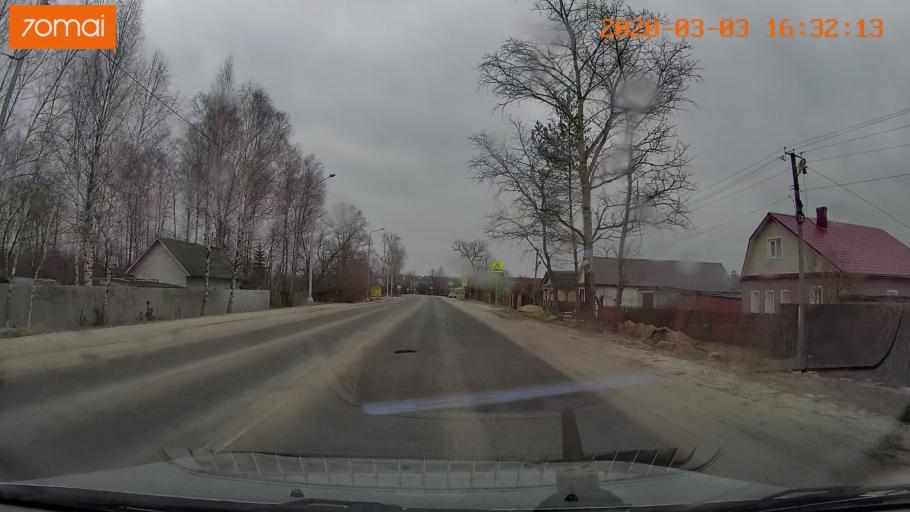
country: RU
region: Moskovskaya
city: Konobeyevo
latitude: 55.4215
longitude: 38.7315
